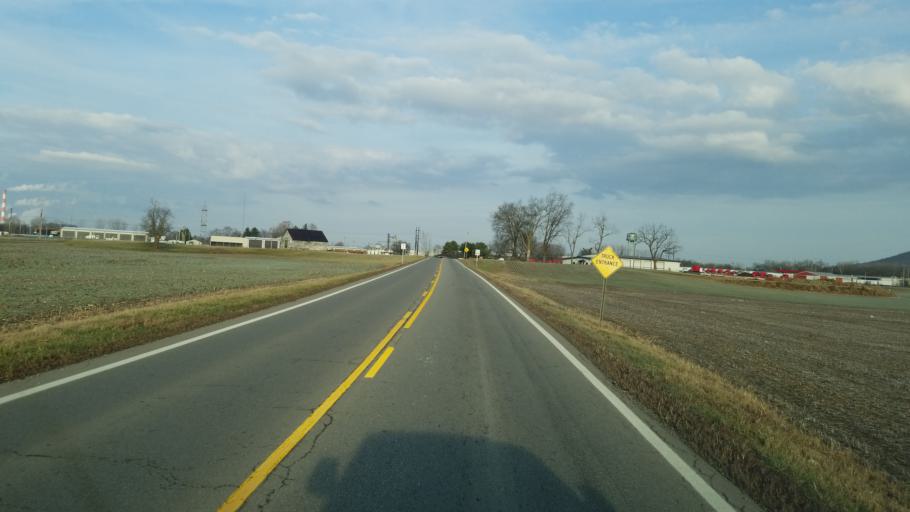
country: US
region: Ohio
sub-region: Ross County
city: Chillicothe
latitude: 39.3171
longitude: -82.9449
